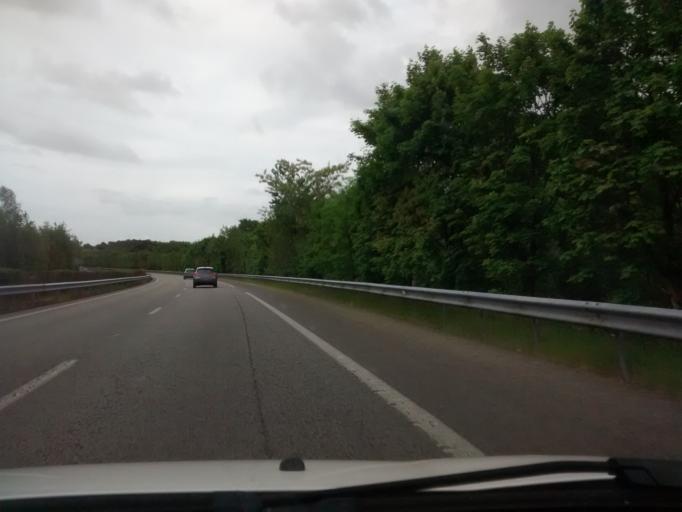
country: FR
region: Brittany
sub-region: Departement du Morbihan
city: Augan
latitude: 47.9258
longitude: -2.2398
